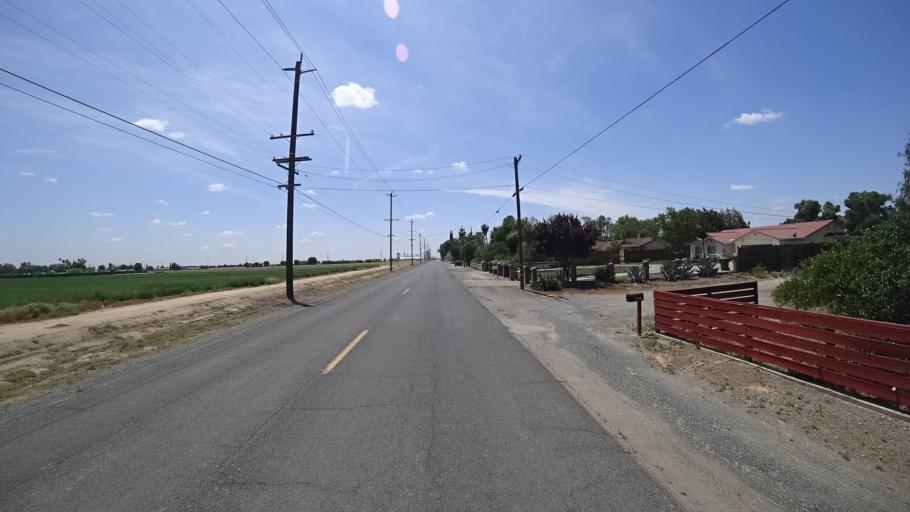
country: US
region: California
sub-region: Kings County
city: Home Garden
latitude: 36.3032
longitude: -119.6459
